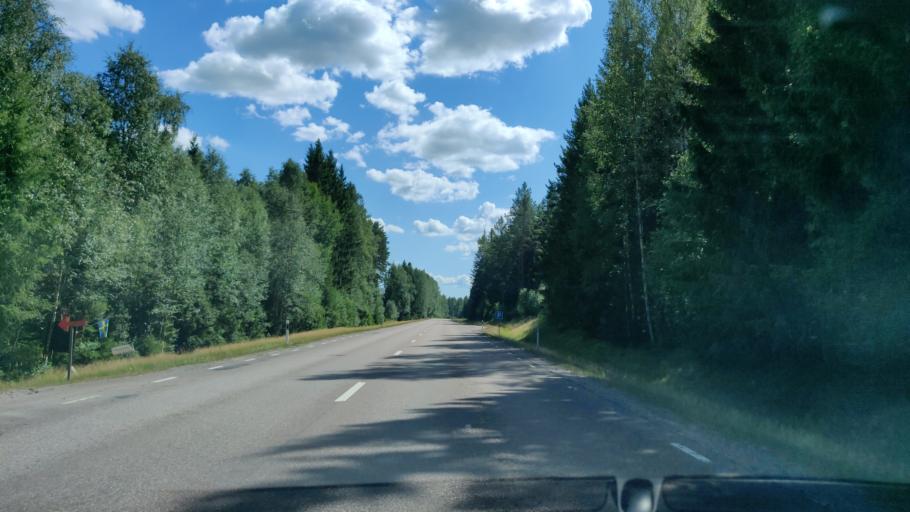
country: SE
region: Vaermland
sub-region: Hagfors Kommun
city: Ekshaerad
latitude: 60.1999
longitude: 13.4944
